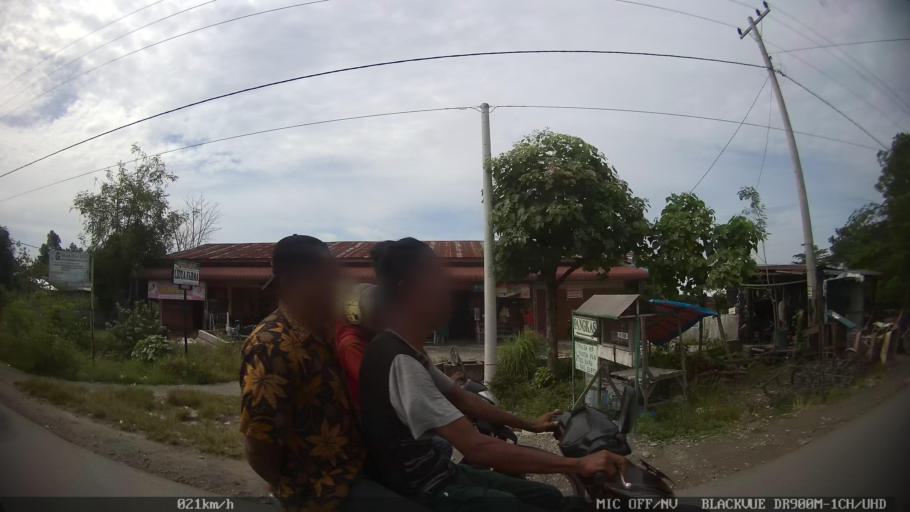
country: ID
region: North Sumatra
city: Medan
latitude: 3.6202
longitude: 98.7562
